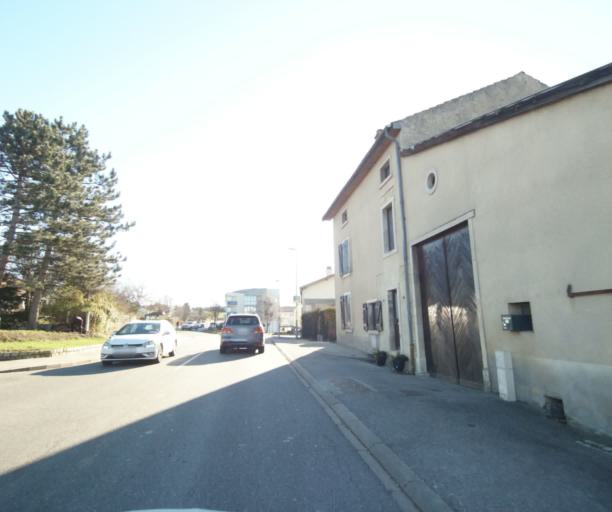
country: FR
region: Lorraine
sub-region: Departement de Meurthe-et-Moselle
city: Fleville-devant-Nancy
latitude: 48.6262
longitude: 6.2062
